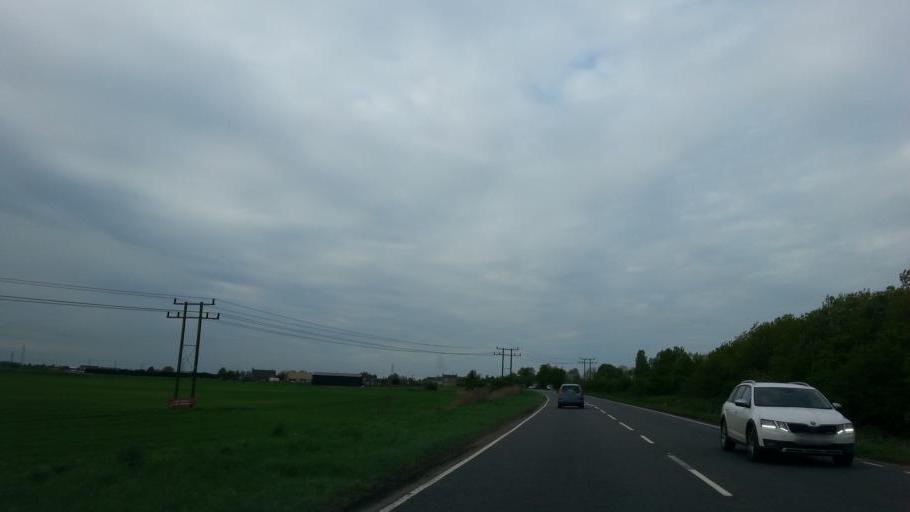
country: GB
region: England
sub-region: Cambridgeshire
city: March
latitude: 52.5409
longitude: 0.0705
